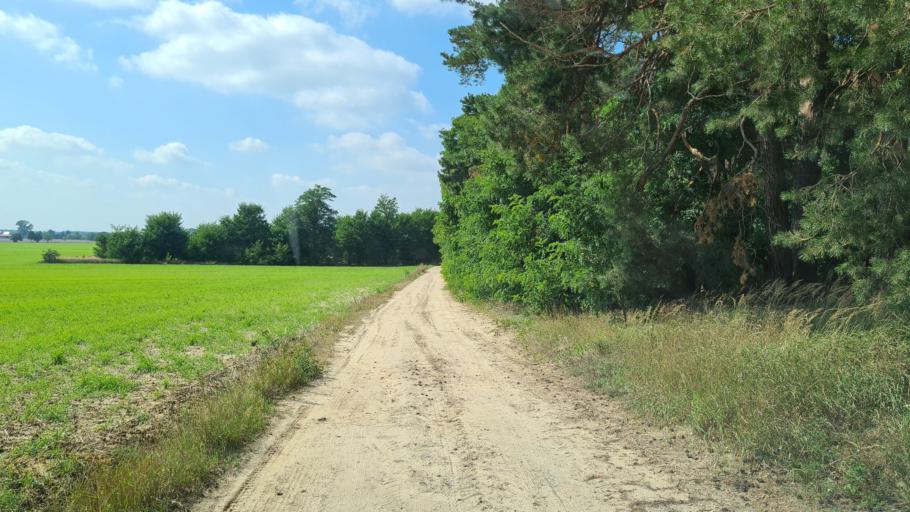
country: DE
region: Brandenburg
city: Sonnewalde
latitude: 51.7364
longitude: 13.6427
